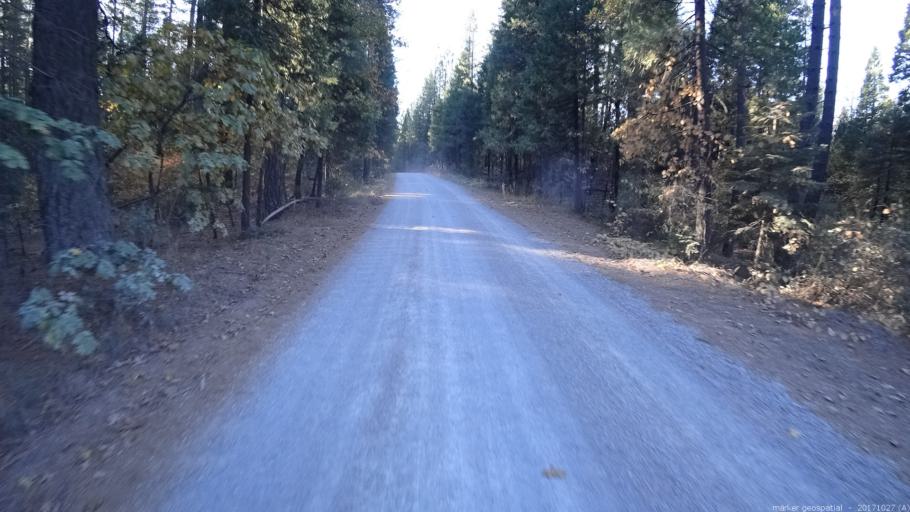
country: US
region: California
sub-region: Shasta County
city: Burney
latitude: 40.9967
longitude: -121.8851
